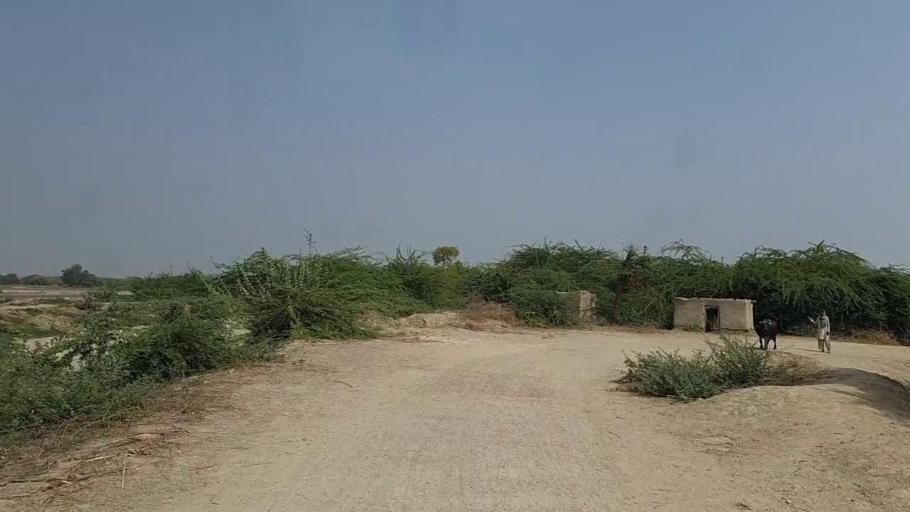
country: PK
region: Sindh
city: Naukot
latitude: 24.8268
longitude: 69.3989
